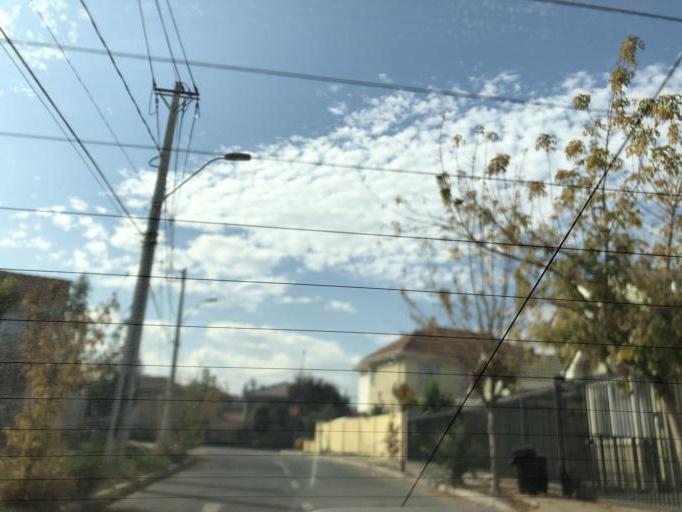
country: CL
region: Santiago Metropolitan
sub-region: Provincia de Cordillera
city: Puente Alto
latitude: -33.5959
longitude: -70.5433
